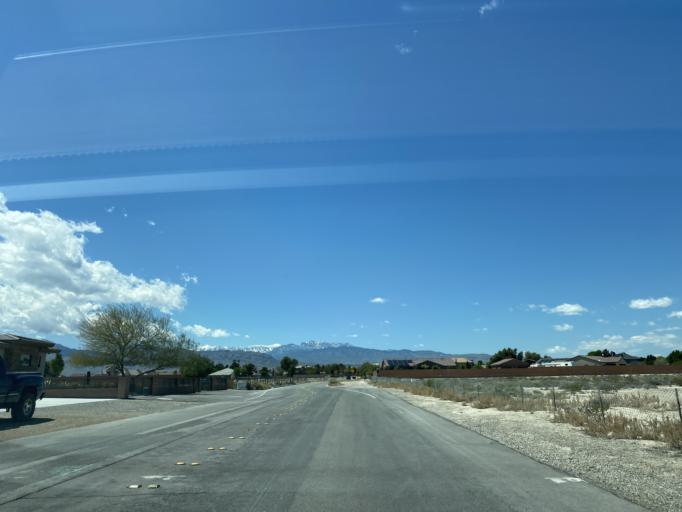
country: US
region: Nevada
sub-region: Clark County
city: North Las Vegas
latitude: 36.3109
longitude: -115.2337
